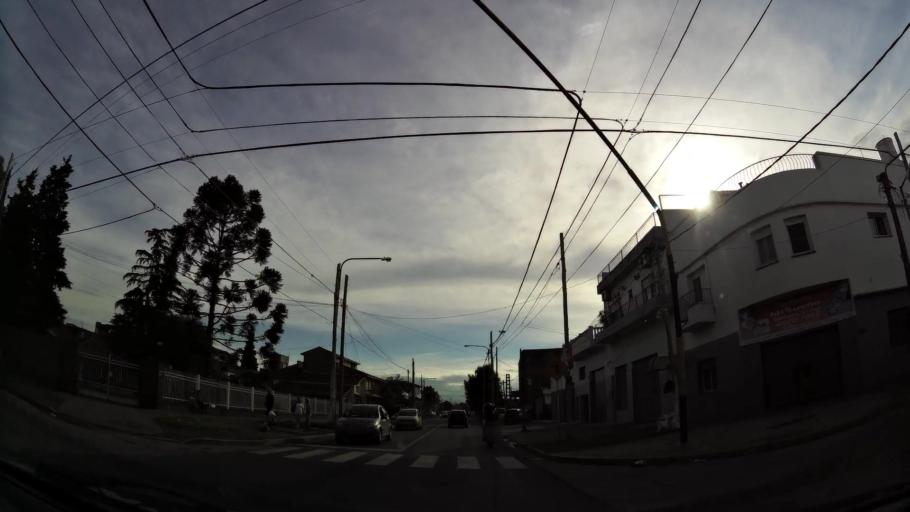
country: AR
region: Buenos Aires
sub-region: Partido de Quilmes
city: Quilmes
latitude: -34.7423
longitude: -58.2709
